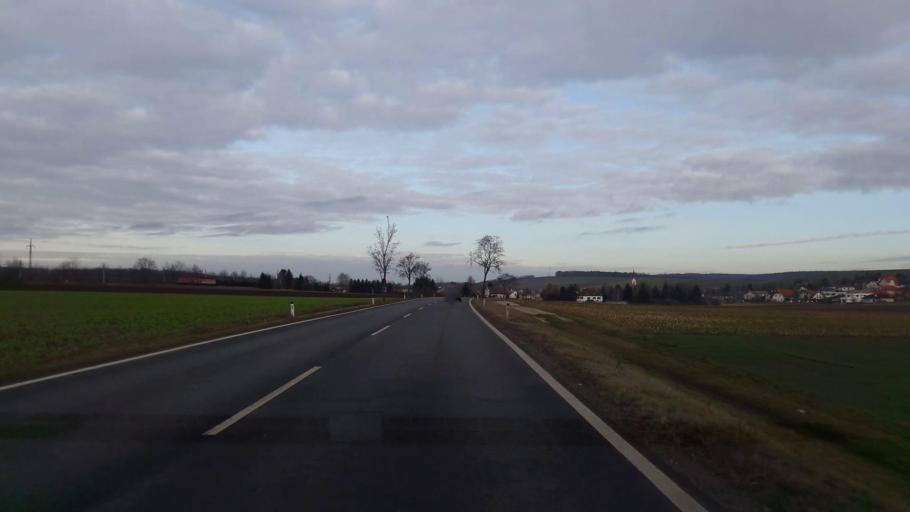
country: AT
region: Lower Austria
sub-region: Politischer Bezirk Mistelbach
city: Mistelbach
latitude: 48.5992
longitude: 16.5432
